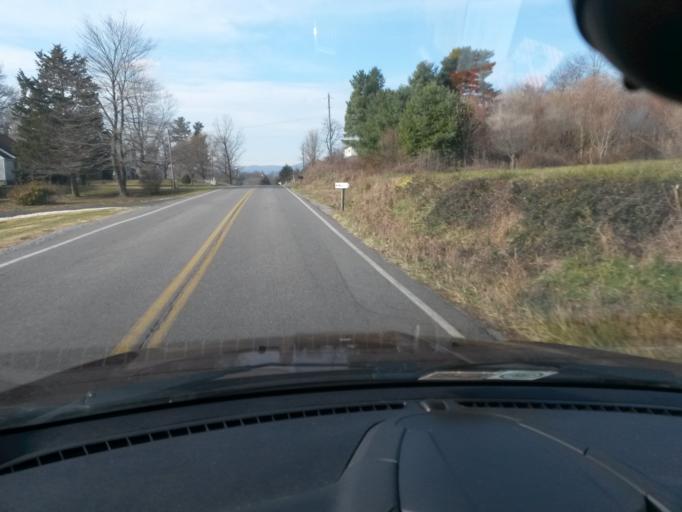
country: US
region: Virginia
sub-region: Botetourt County
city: Daleville
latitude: 37.4564
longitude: -79.9423
